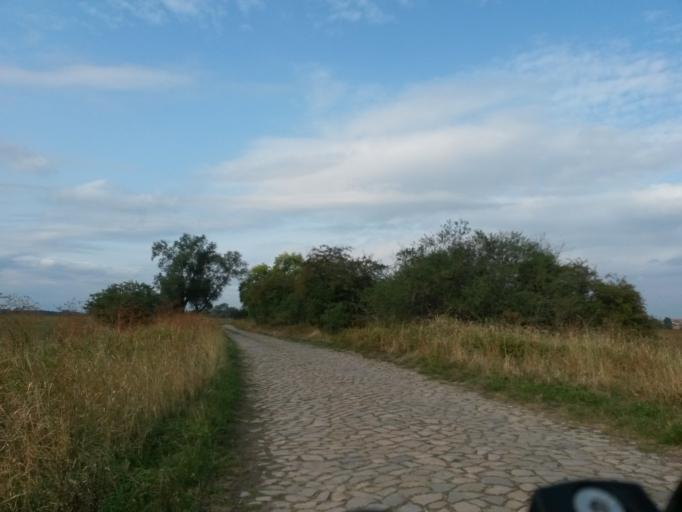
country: DE
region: Saxony-Anhalt
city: Tangermunde
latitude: 52.5375
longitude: 11.9943
